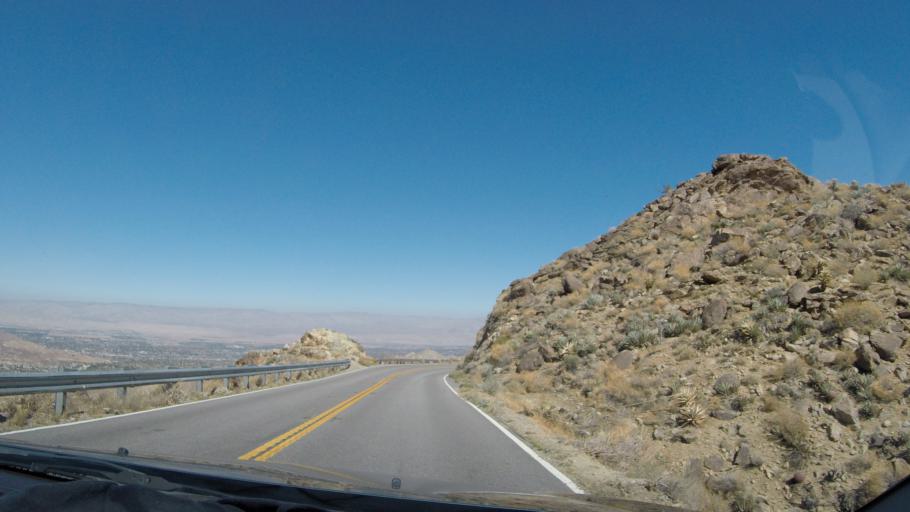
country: US
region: California
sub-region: Riverside County
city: Palm Desert
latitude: 33.6492
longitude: -116.4057
